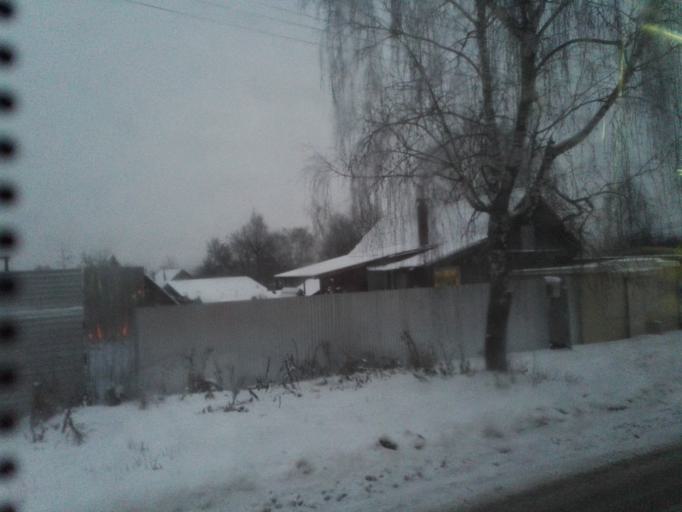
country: RU
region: Tula
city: Tula
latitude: 54.1644
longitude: 37.6076
